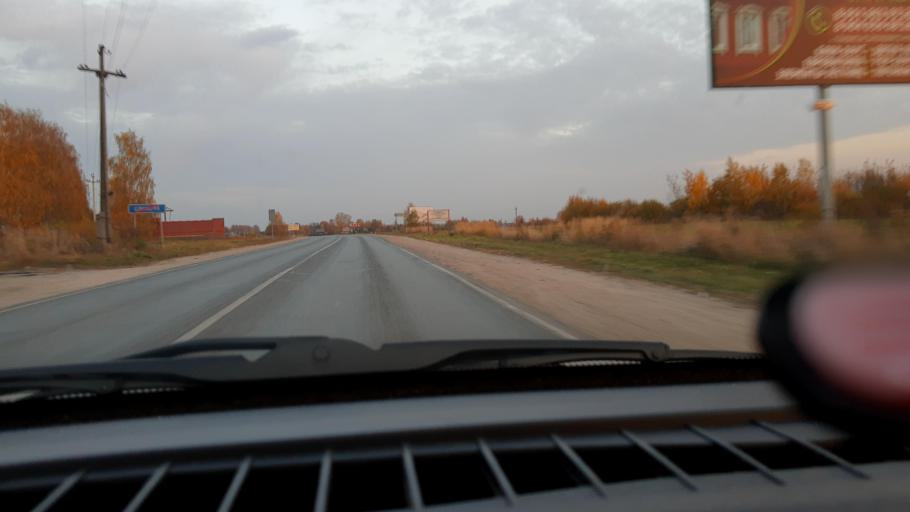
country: RU
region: Nizjnij Novgorod
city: Gorodets
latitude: 56.6393
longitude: 43.5059
